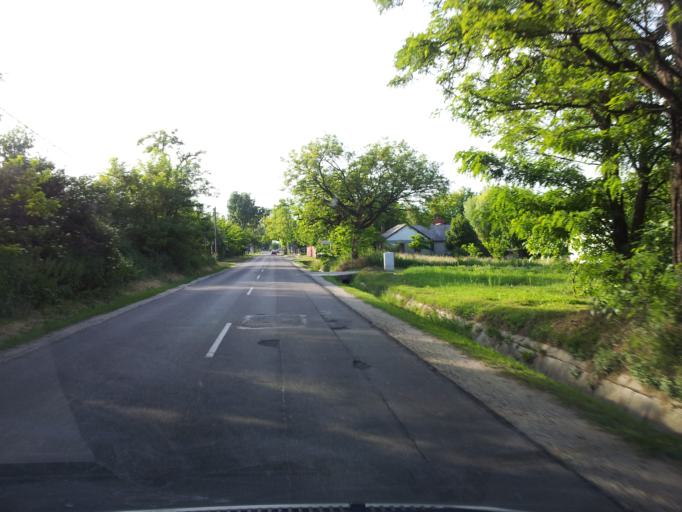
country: HU
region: Komarom-Esztergom
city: Esztergom
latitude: 47.7721
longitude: 18.7564
